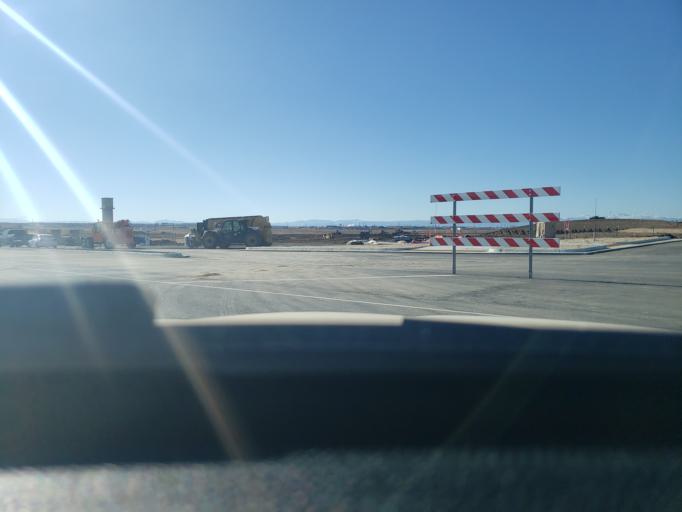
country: US
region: Colorado
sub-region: Adams County
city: Aurora
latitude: 39.7692
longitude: -104.7126
